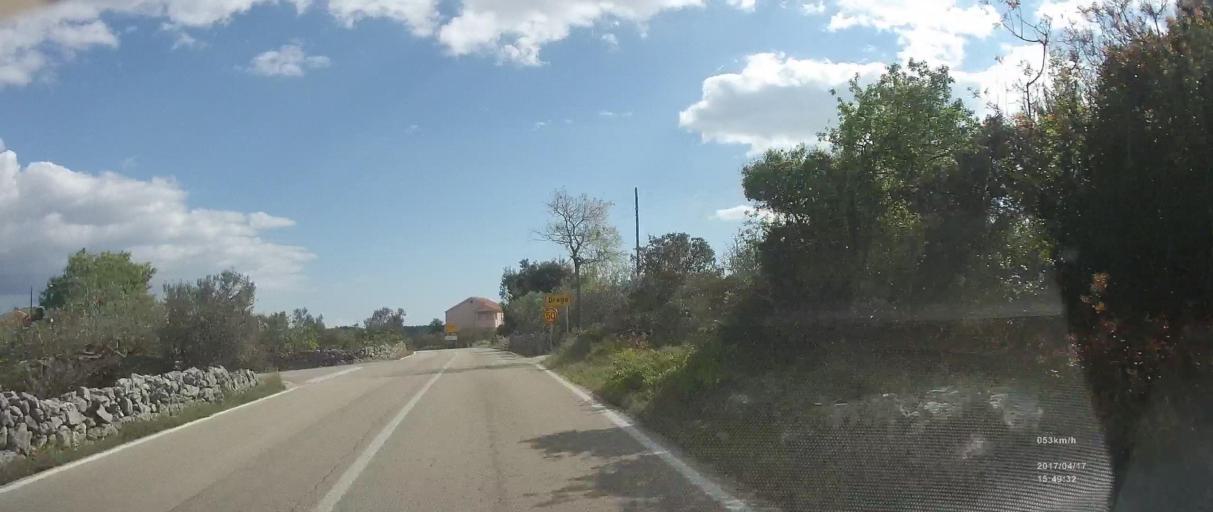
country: HR
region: Sibensko-Kniniska
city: Primosten
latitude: 43.6133
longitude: 15.9762
